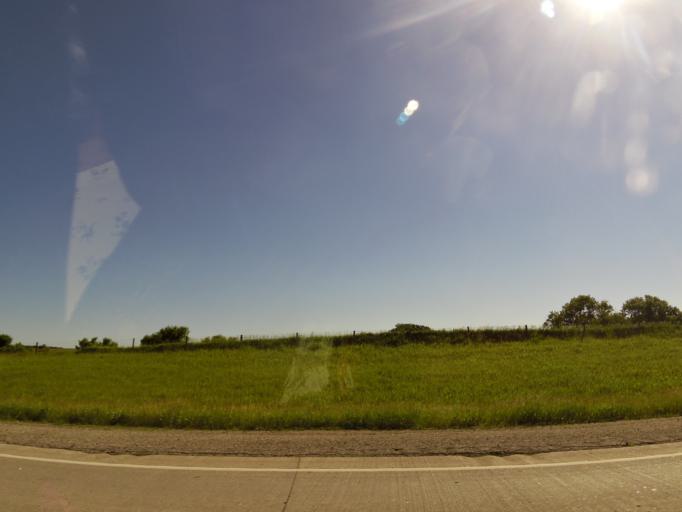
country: US
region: Minnesota
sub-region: Otter Tail County
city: Fergus Falls
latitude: 46.3799
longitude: -96.1829
